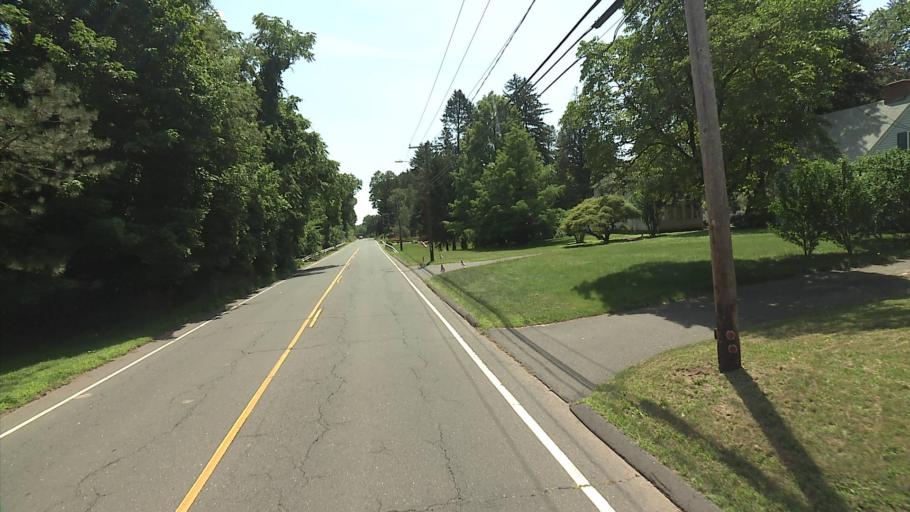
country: US
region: Connecticut
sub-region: Hartford County
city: New Britain
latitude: 41.6435
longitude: -72.7858
